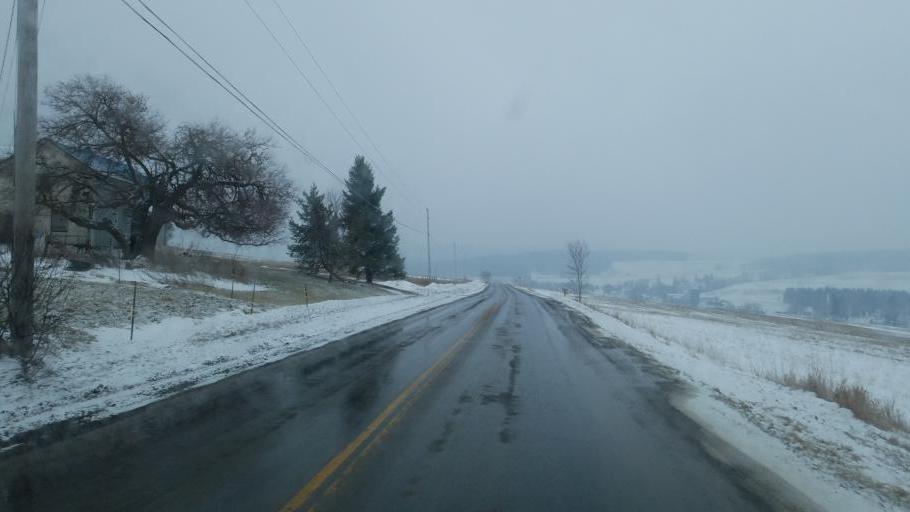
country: US
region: New York
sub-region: Steuben County
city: Canisteo
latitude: 42.1321
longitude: -77.5019
